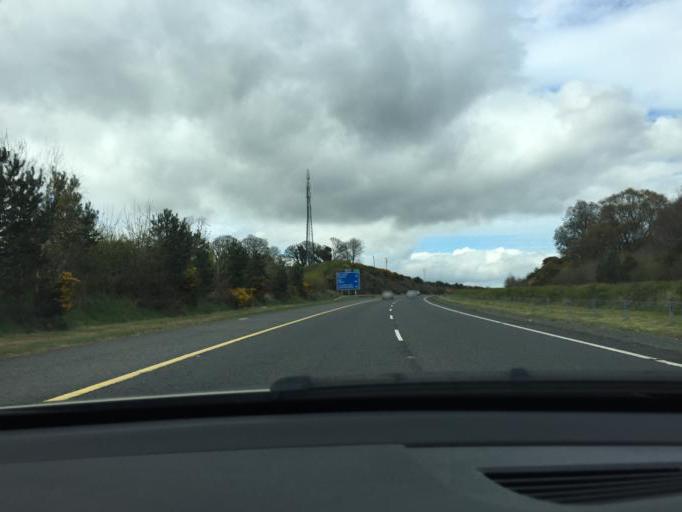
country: IE
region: Leinster
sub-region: Wicklow
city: Ashford
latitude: 53.0130
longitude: -6.0995
